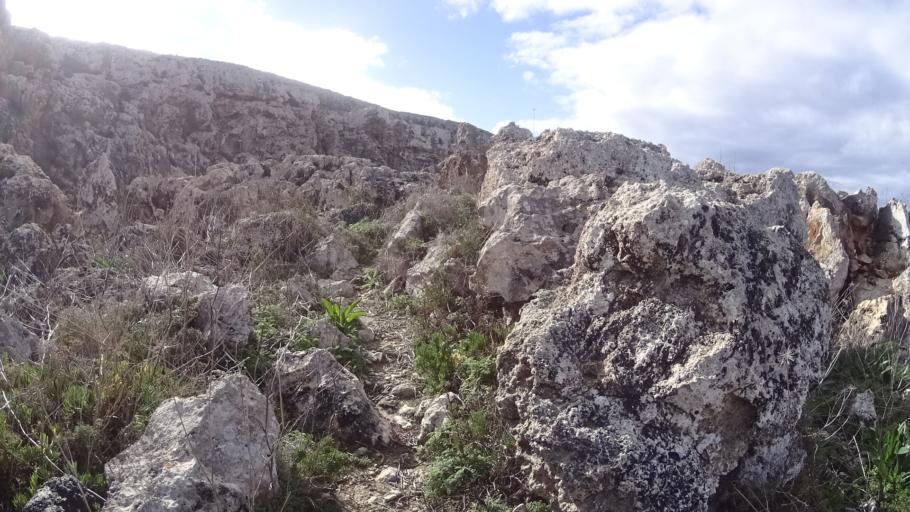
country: MT
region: Il-Mellieha
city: Mellieha
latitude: 35.9805
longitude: 14.3290
